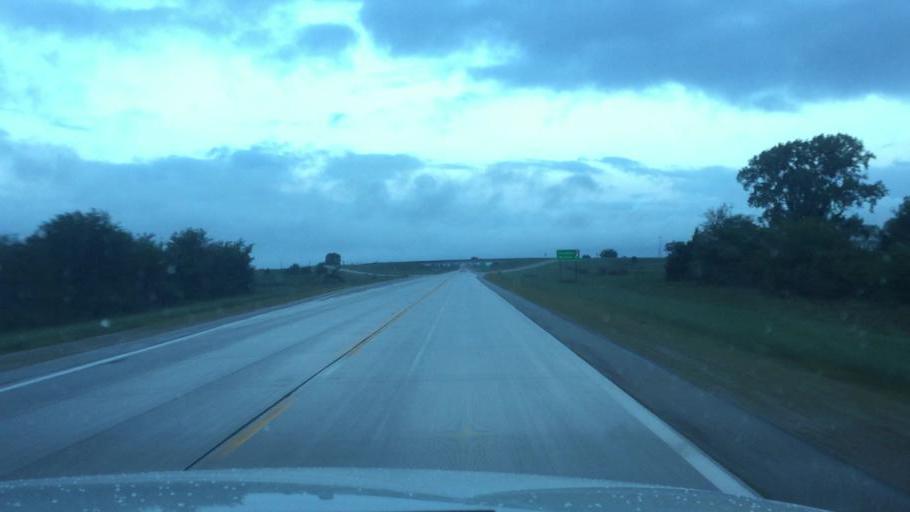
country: US
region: Kansas
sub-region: Neosho County
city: Chanute
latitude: 37.7290
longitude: -95.4656
